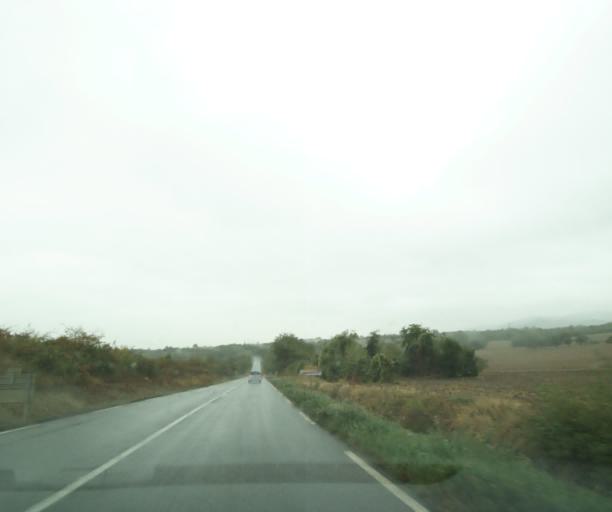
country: FR
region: Auvergne
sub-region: Departement du Puy-de-Dome
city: Cebazat
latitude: 45.8482
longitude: 3.1041
